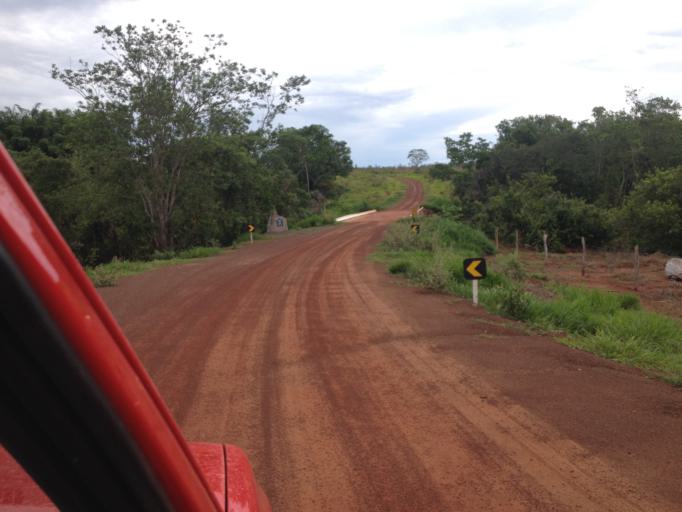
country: BR
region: Goias
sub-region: Cacu
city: Cacu
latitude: -18.4298
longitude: -51.5401
